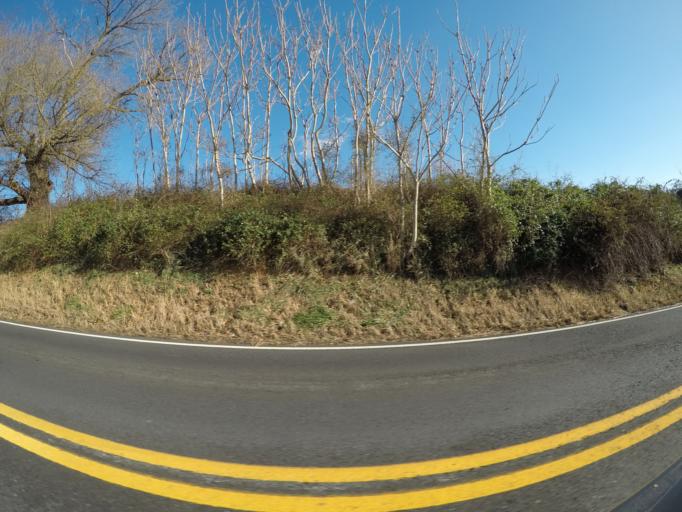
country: US
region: Maryland
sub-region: Harford County
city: South Bel Air
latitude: 39.6150
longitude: -76.2597
